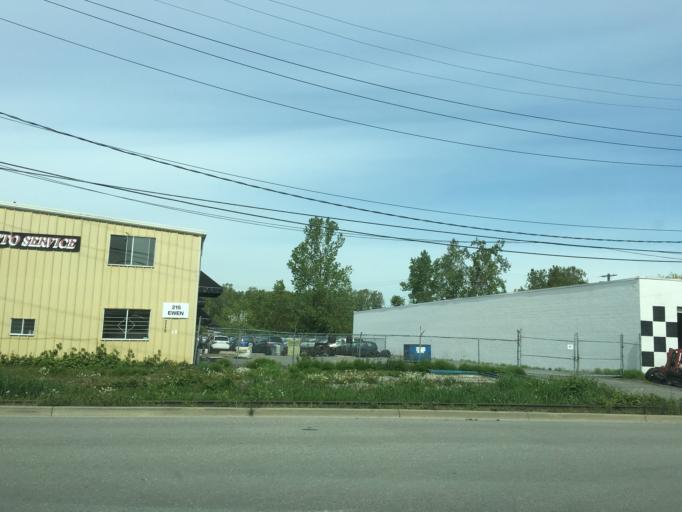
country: CA
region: British Columbia
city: New Westminster
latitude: 49.1940
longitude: -122.9279
